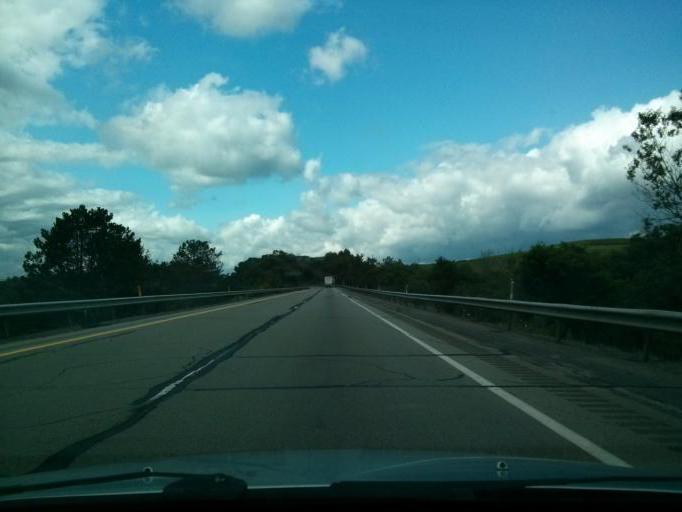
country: US
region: Pennsylvania
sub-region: Jefferson County
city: Brookville
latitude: 41.1697
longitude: -79.0276
